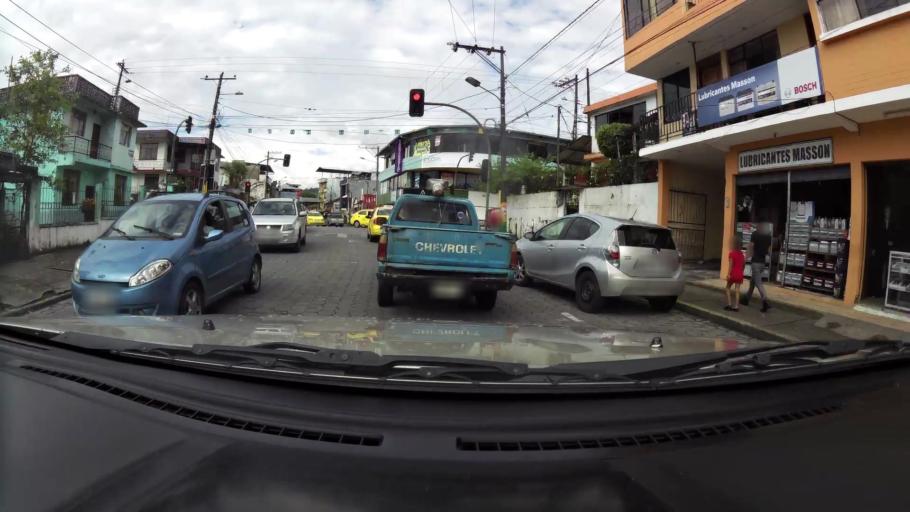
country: EC
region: Pastaza
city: Puyo
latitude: -1.4857
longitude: -78.0037
